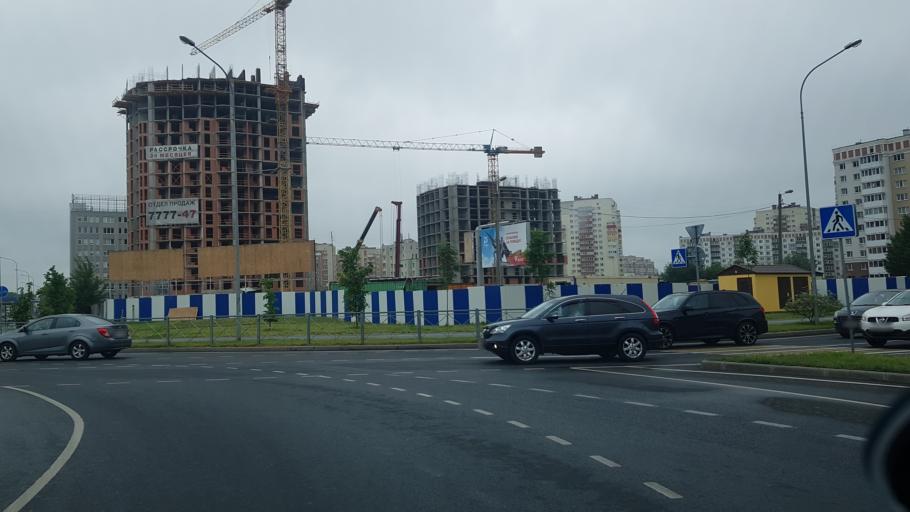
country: RU
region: Kaliningrad
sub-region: Gorod Kaliningrad
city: Kaliningrad
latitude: 54.7369
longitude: 20.4933
